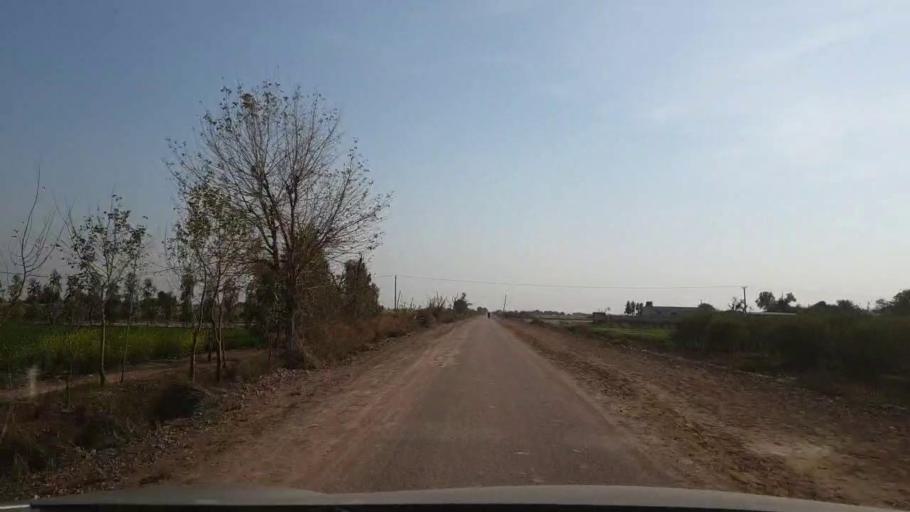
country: PK
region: Sindh
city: Berani
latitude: 25.7293
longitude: 68.8066
